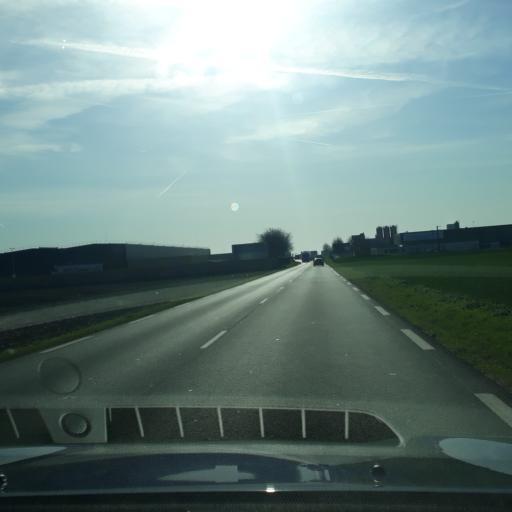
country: FR
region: Ile-de-France
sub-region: Departement de l'Essonne
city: Corbreuse
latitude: 48.4540
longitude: 1.9201
